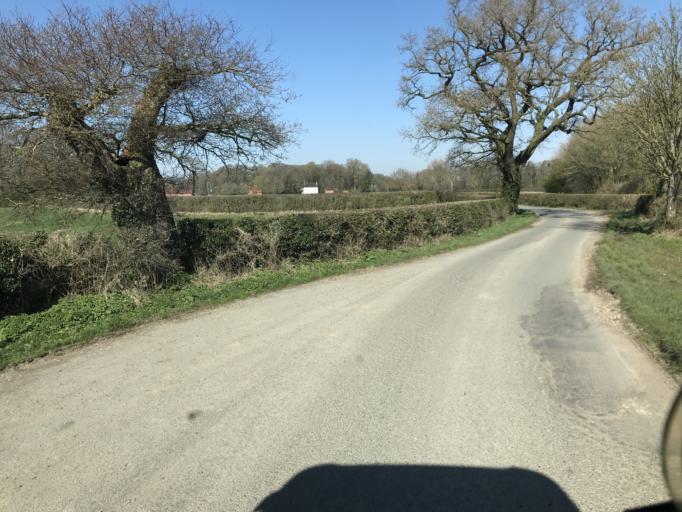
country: GB
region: England
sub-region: Cheshire West and Chester
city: Aldford
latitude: 53.1280
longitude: -2.8585
